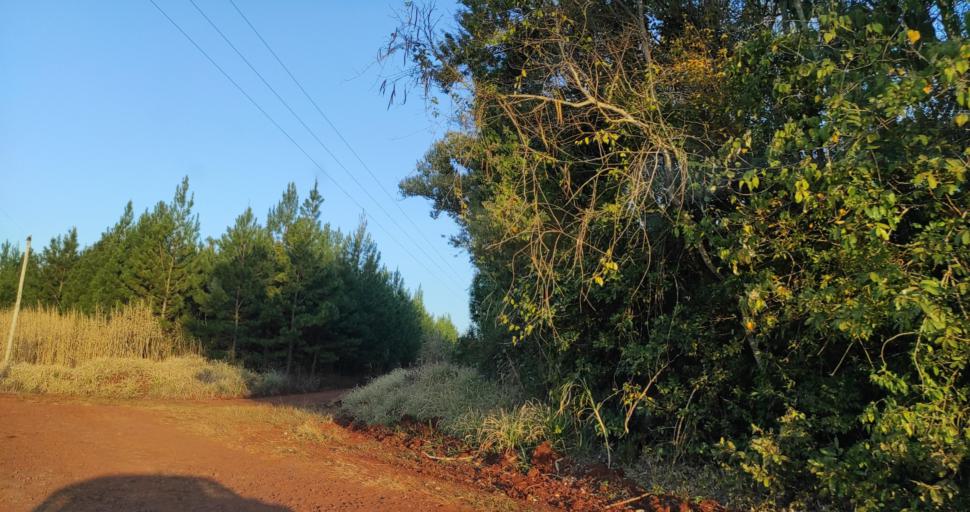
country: AR
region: Misiones
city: Capiovi
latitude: -26.8810
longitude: -55.1227
